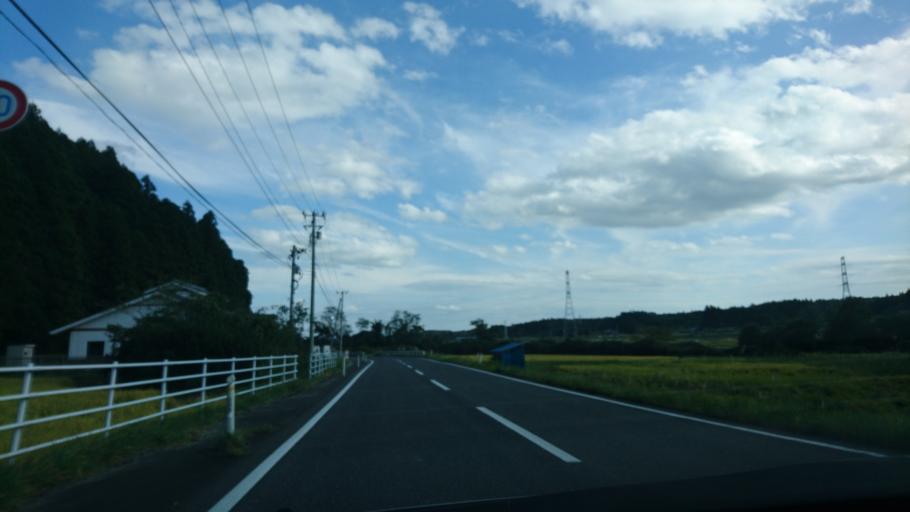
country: JP
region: Iwate
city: Ichinoseki
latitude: 38.8638
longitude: 141.1317
